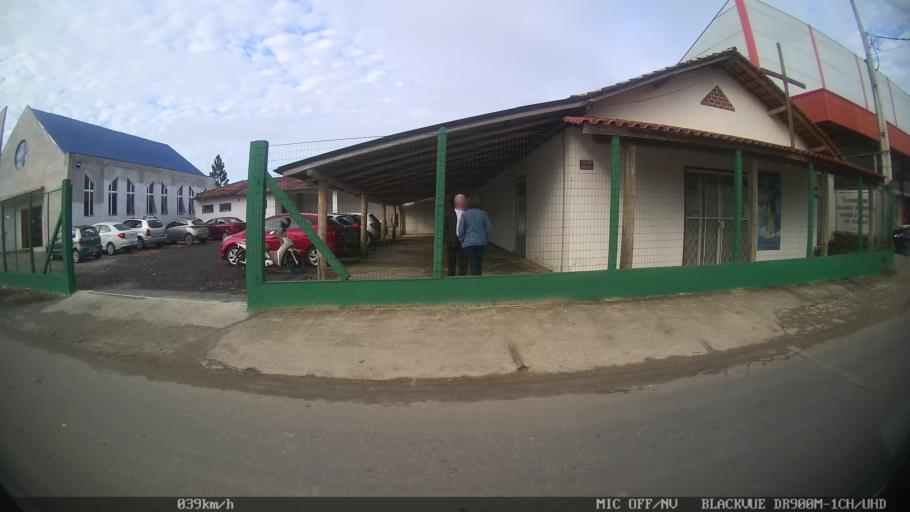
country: BR
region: Santa Catarina
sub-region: Barra Velha
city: Barra Velha
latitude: -26.6212
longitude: -48.7068
